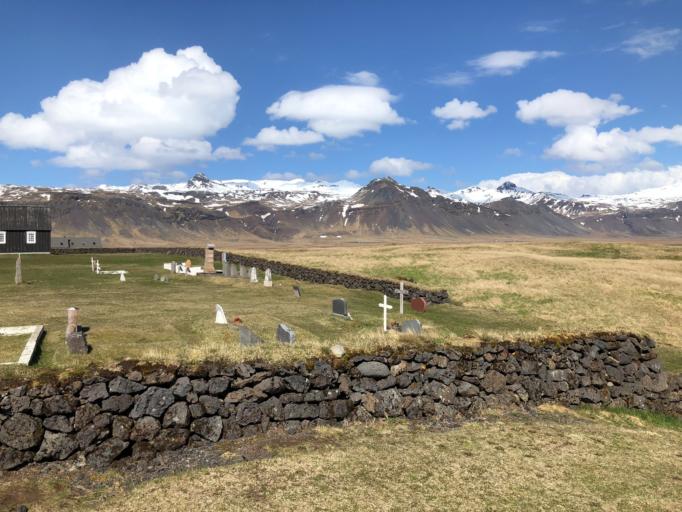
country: IS
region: West
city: Olafsvik
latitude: 64.8210
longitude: -23.3838
